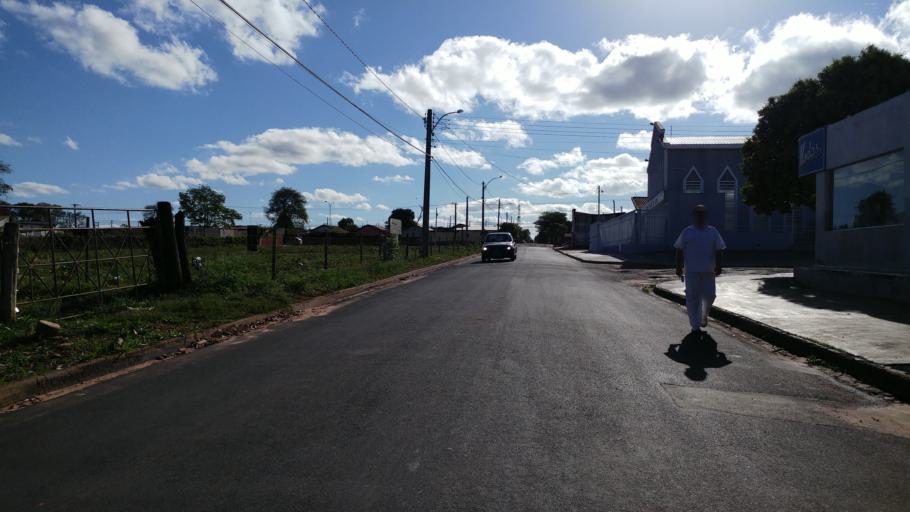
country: BR
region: Sao Paulo
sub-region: Paraguacu Paulista
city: Paraguacu Paulista
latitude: -22.4335
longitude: -50.5784
